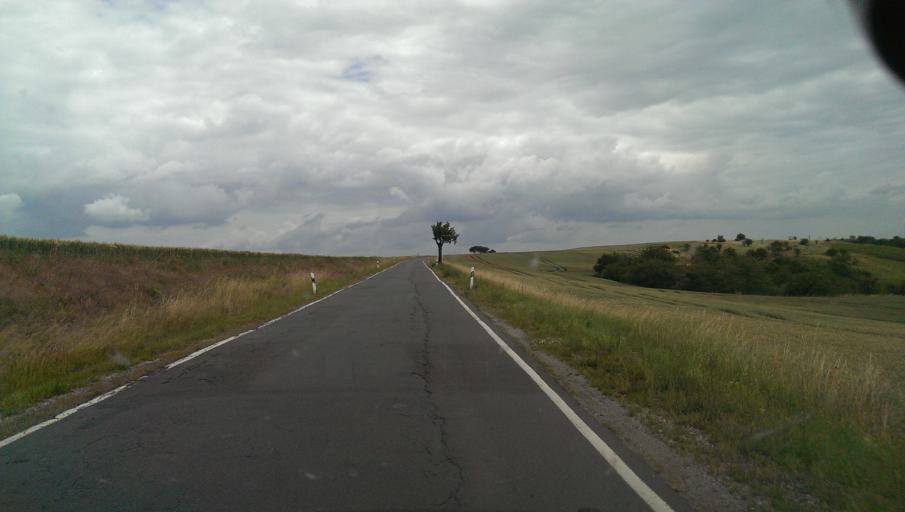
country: DE
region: Saxony-Anhalt
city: Farnstadt
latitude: 51.4328
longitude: 11.6004
